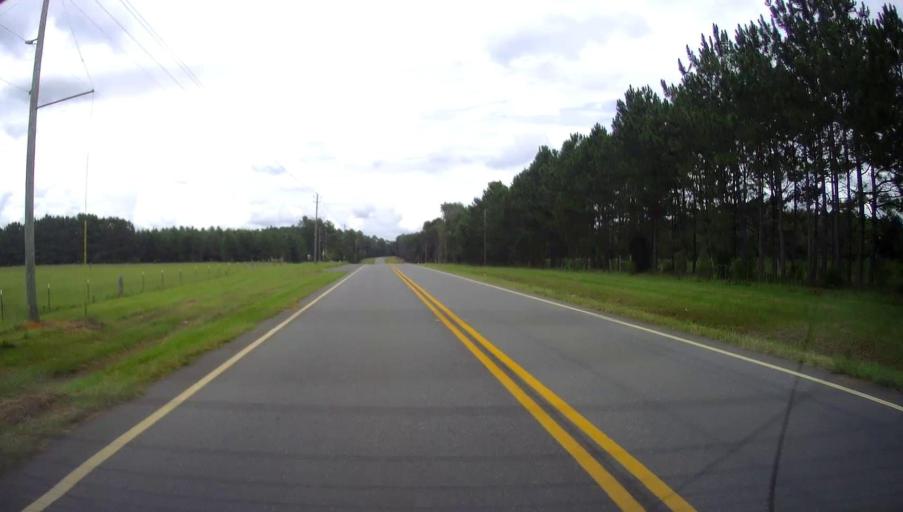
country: US
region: Georgia
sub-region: Schley County
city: Ellaville
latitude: 32.2505
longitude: -84.2809
